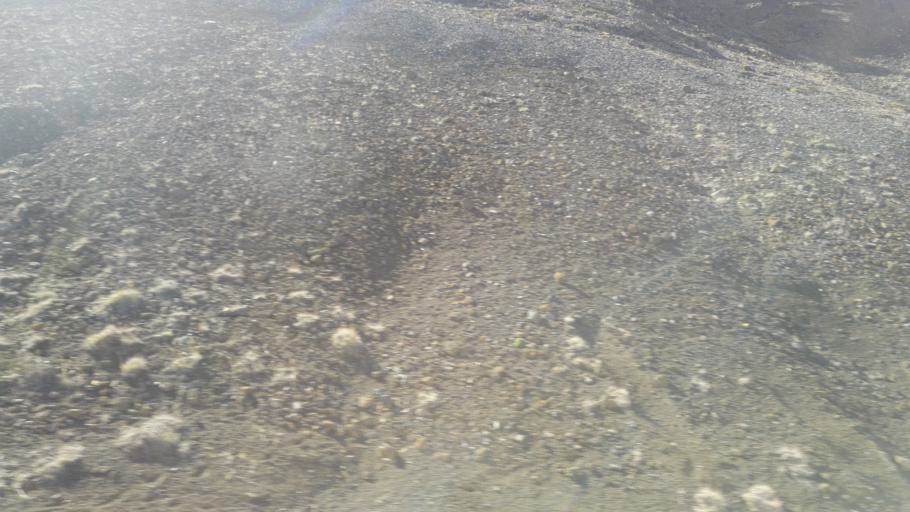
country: IS
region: South
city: Hveragerdi
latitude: 64.1221
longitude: -21.3035
